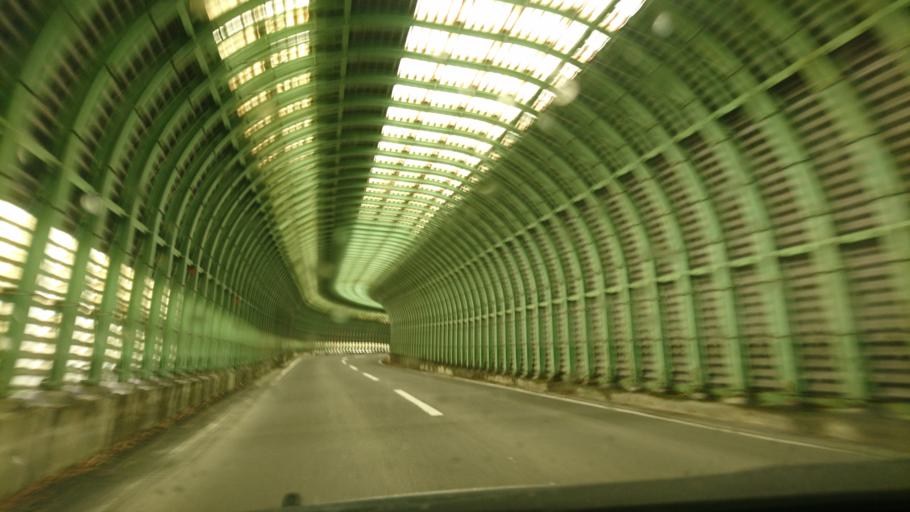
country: JP
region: Iwate
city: Ichinoseki
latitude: 38.9397
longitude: 140.8270
